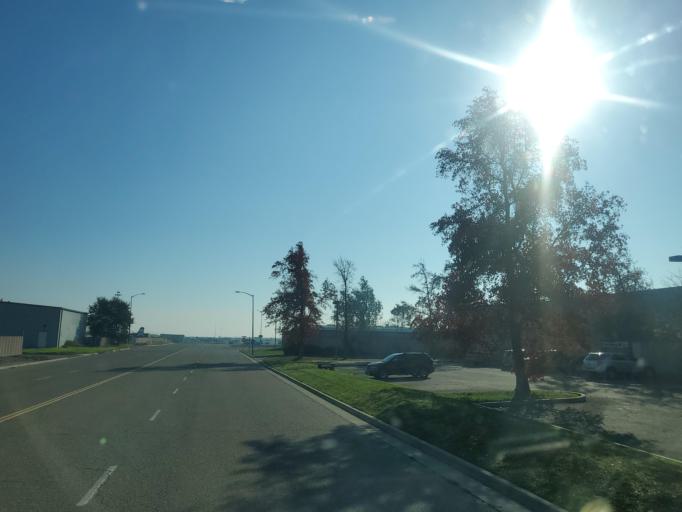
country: US
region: California
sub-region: San Joaquin County
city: French Camp
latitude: 37.8909
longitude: -121.2437
